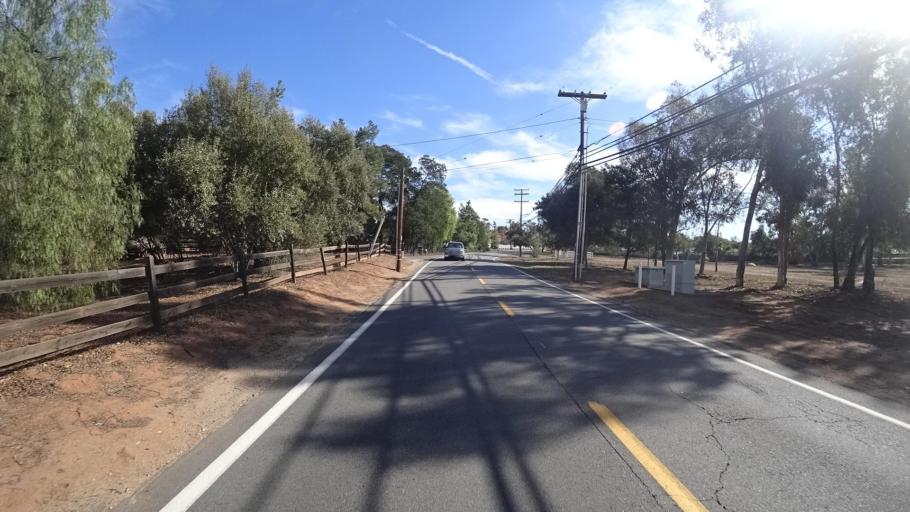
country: US
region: California
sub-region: San Diego County
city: Harbison Canyon
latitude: 32.8188
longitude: -116.7962
